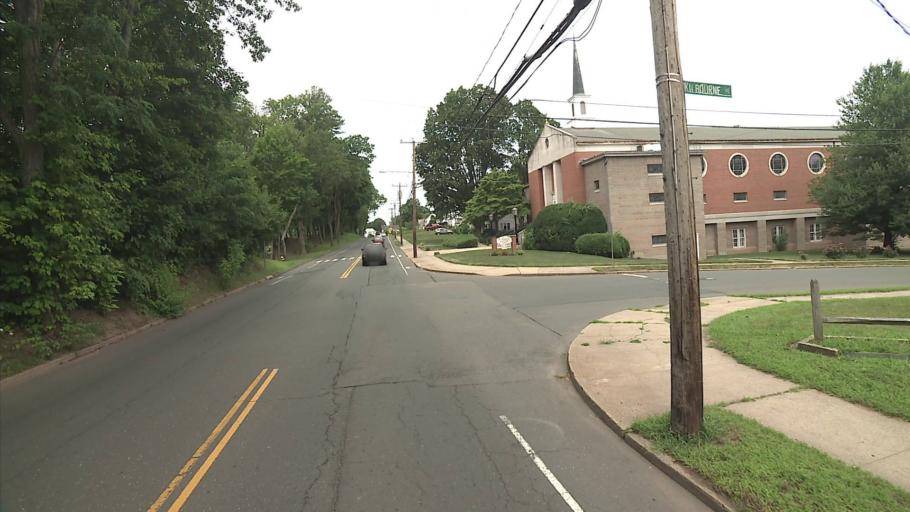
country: US
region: Connecticut
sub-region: Hartford County
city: New Britain
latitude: 41.6932
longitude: -72.7716
